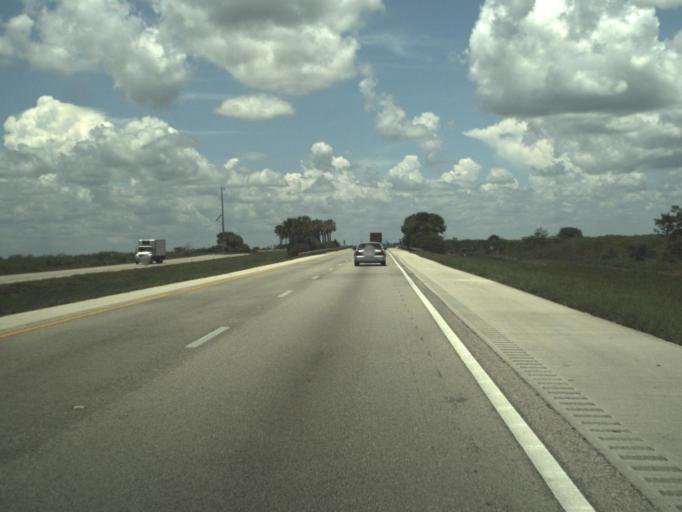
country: US
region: Florida
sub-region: Broward County
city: Weston
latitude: 26.1465
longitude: -80.5924
